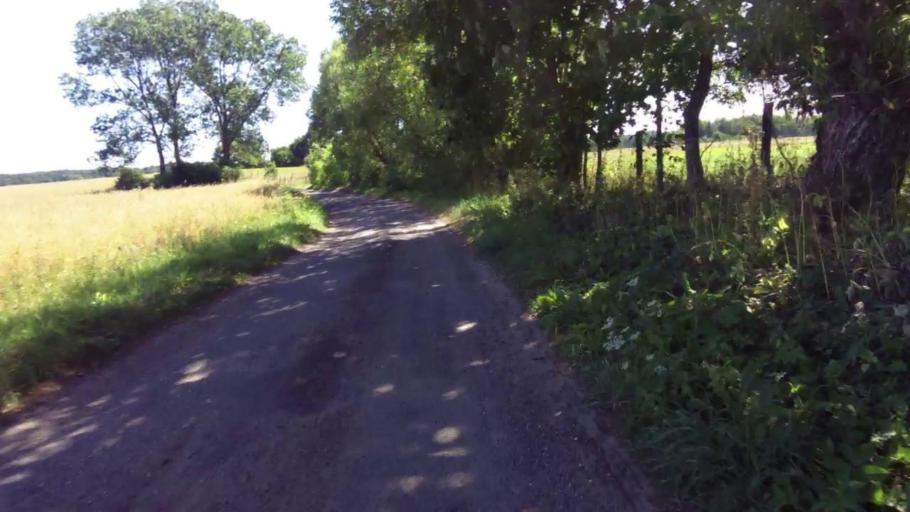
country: PL
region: West Pomeranian Voivodeship
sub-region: Powiat drawski
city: Czaplinek
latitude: 53.5252
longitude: 16.1553
